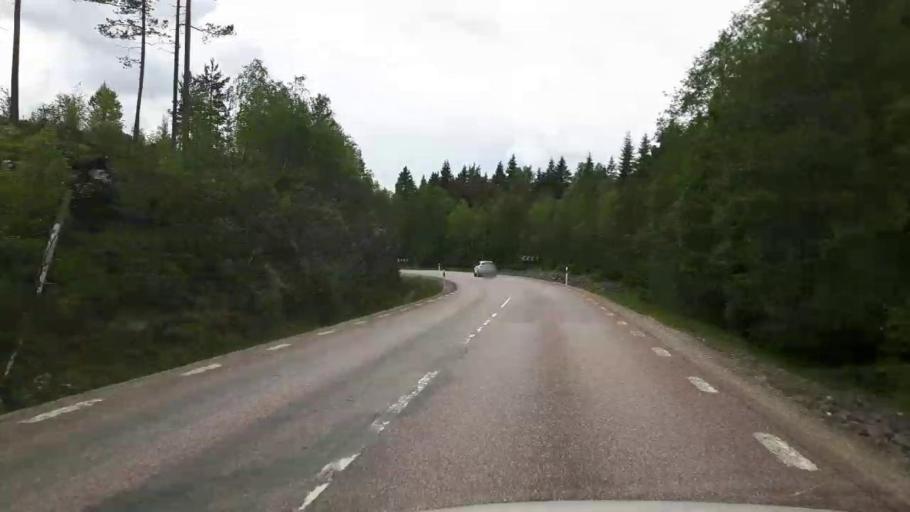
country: SE
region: Vaestmanland
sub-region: Norbergs Kommun
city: Norberg
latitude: 60.1272
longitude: 15.9207
